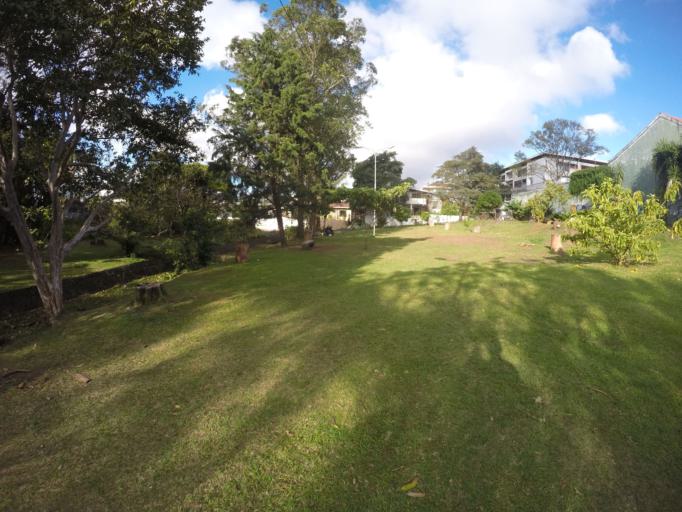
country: CR
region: San Jose
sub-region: Canton de Goicoechea
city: Guadalupe
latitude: 9.9376
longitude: -84.0597
